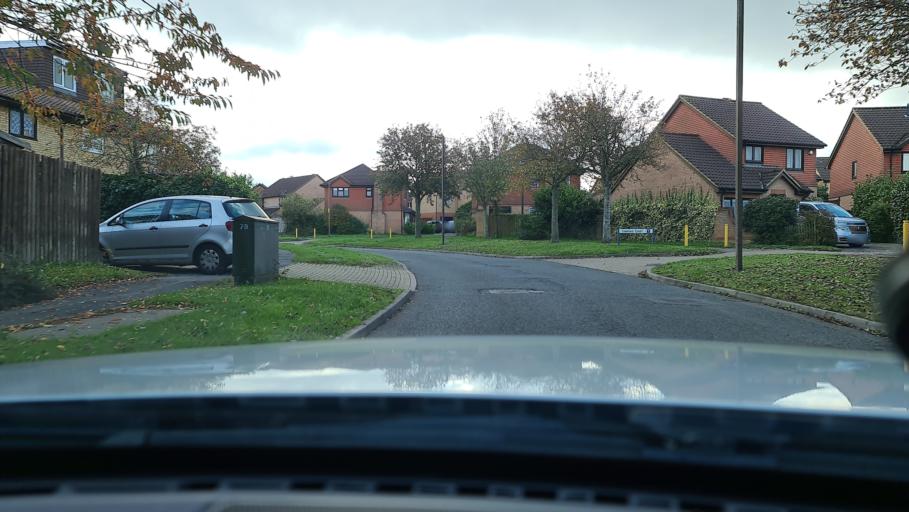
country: GB
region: England
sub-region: Milton Keynes
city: Simpson
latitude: 52.0231
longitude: -0.6947
